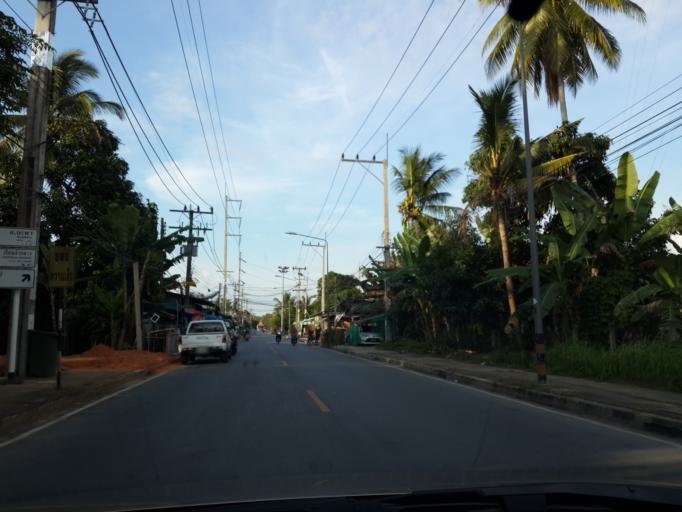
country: TH
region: Yala
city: Yala
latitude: 6.5314
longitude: 101.2623
